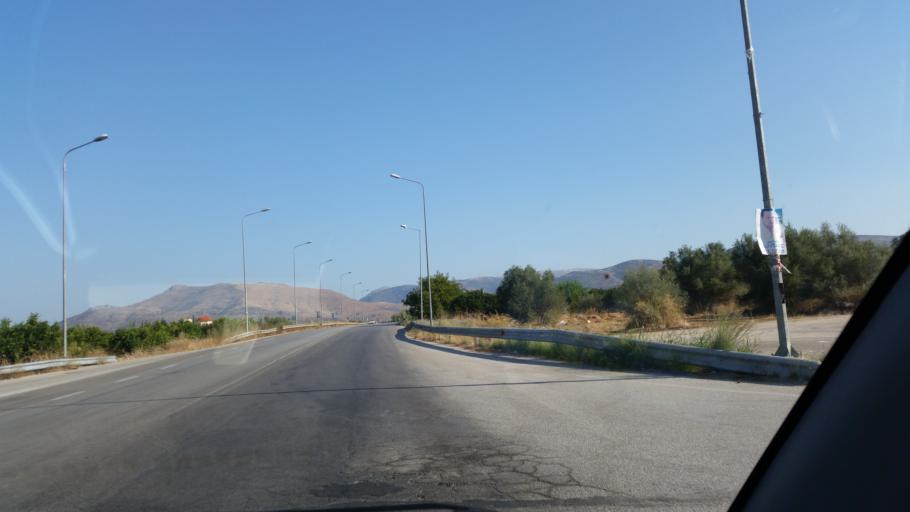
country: GR
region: Peloponnese
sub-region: Nomos Argolidos
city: Ayia Trias
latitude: 37.6334
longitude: 22.8172
